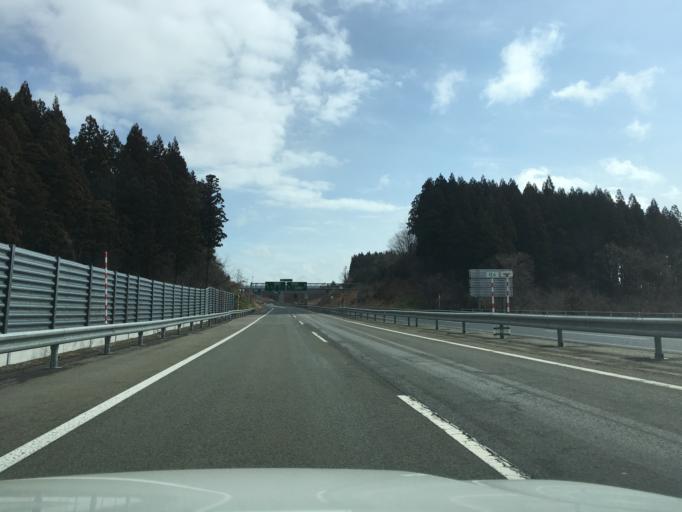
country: JP
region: Akita
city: Akita
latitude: 39.6381
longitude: 140.2038
